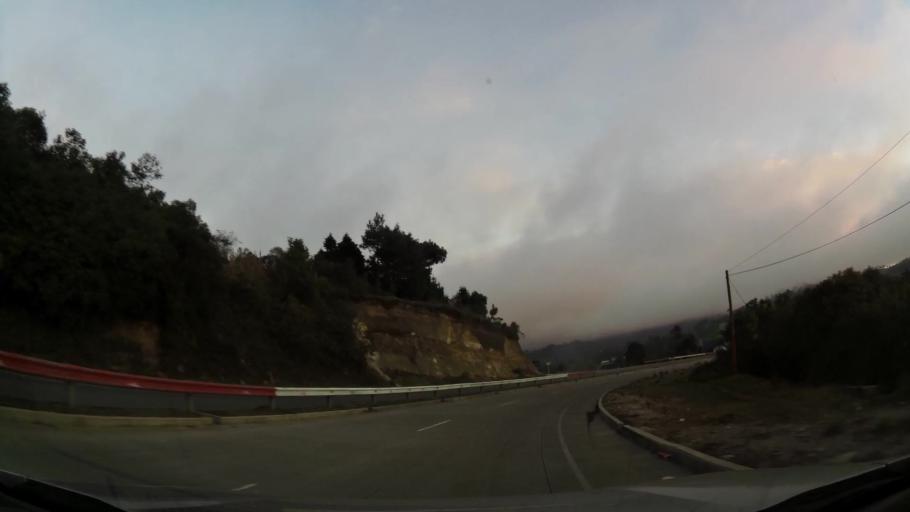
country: GT
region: Solola
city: Concepcion
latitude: 14.8339
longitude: -91.0951
